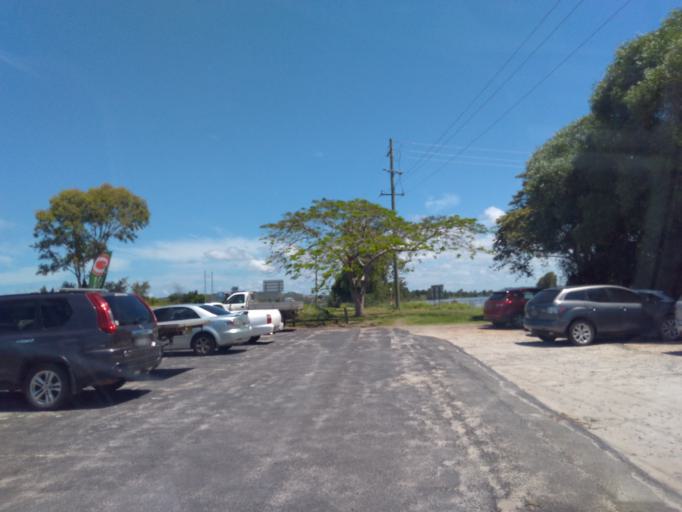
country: AU
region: New South Wales
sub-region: Clarence Valley
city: Maclean
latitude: -29.4731
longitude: 153.2051
